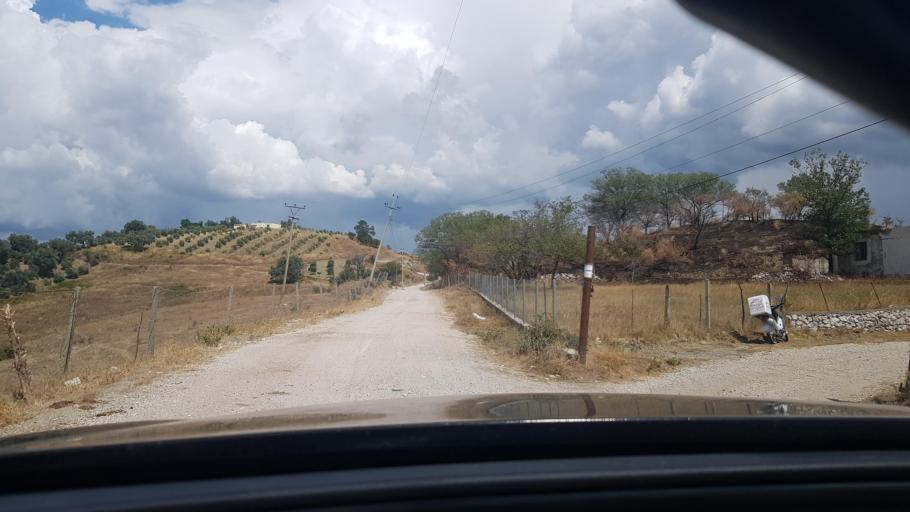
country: AL
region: Durres
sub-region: Rrethi i Durresit
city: Rrashbull
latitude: 41.2924
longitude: 19.5411
